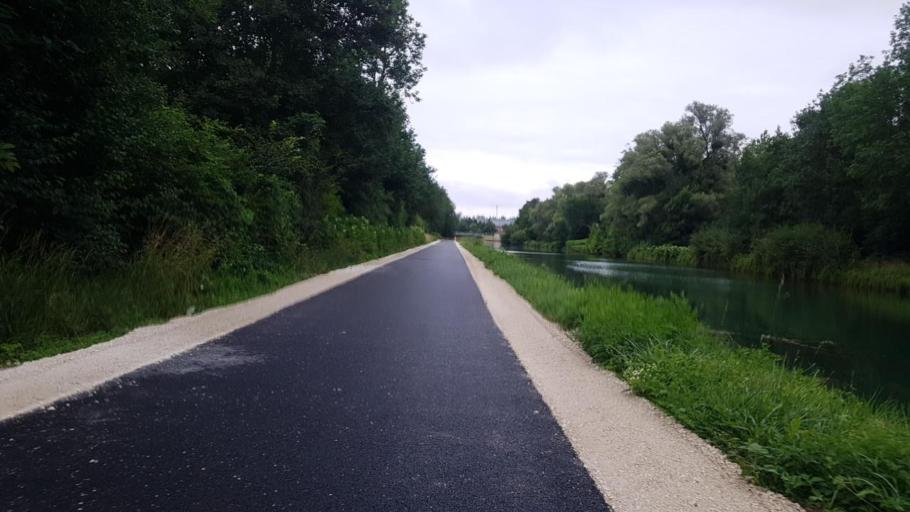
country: FR
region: Champagne-Ardenne
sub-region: Departement de la Marne
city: Vitry-le-Francois
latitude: 48.8302
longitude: 4.5130
